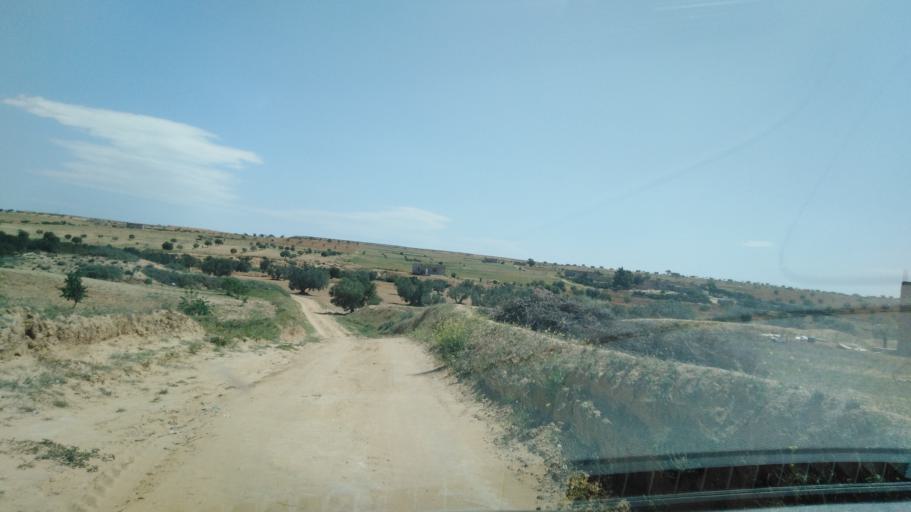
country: TN
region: Safaqis
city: Sfax
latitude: 34.7795
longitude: 10.5262
